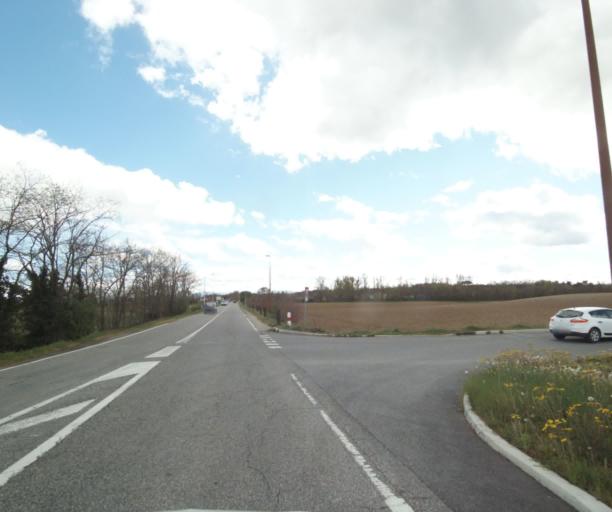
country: FR
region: Midi-Pyrenees
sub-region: Departement de l'Ariege
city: Saverdun
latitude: 43.2502
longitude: 1.5668
